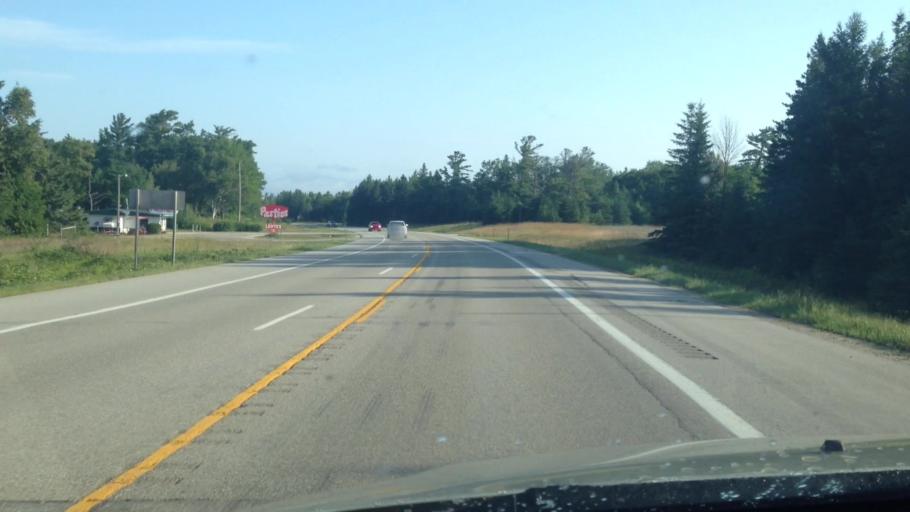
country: US
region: Michigan
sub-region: Mackinac County
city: Saint Ignace
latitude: 45.8931
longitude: -84.8326
